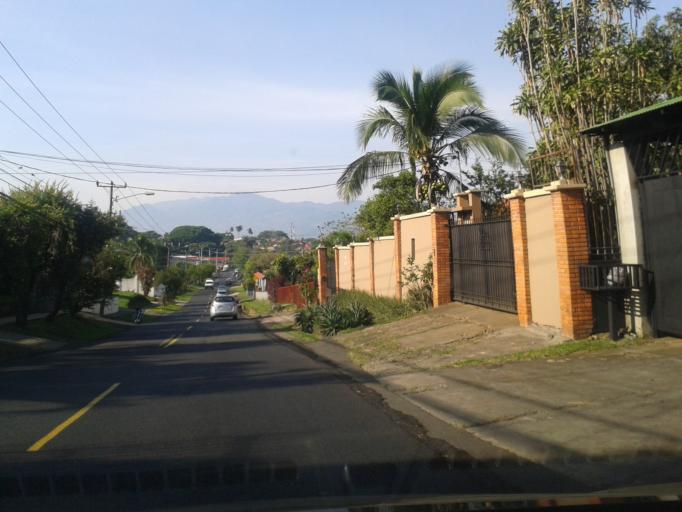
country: CR
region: Heredia
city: Llorente
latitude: 10.0114
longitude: -84.1521
